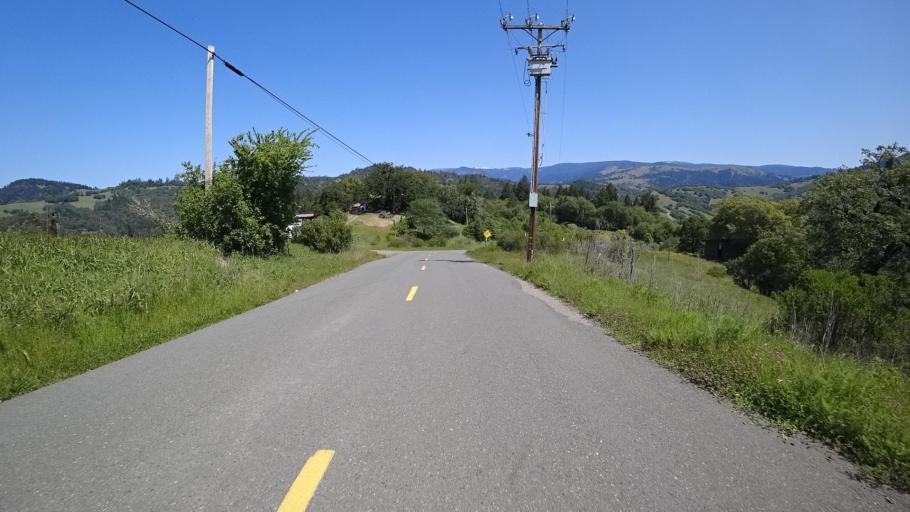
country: US
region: California
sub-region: Humboldt County
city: Redway
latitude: 40.1678
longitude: -123.6111
